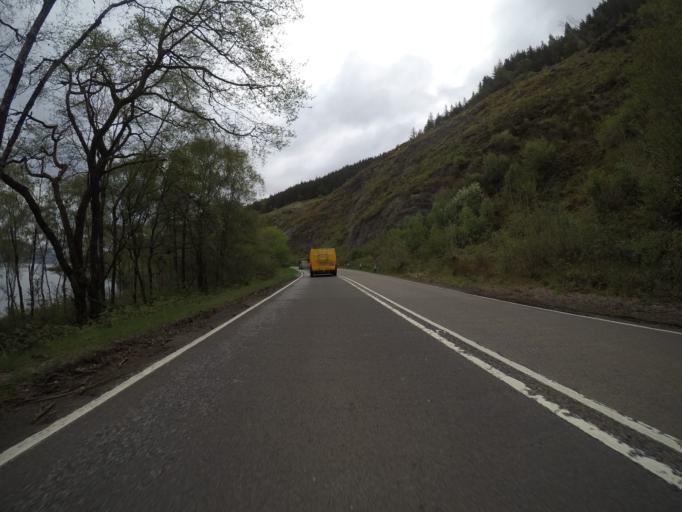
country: GB
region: Scotland
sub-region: Highland
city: Fort William
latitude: 56.7382
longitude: -5.2115
